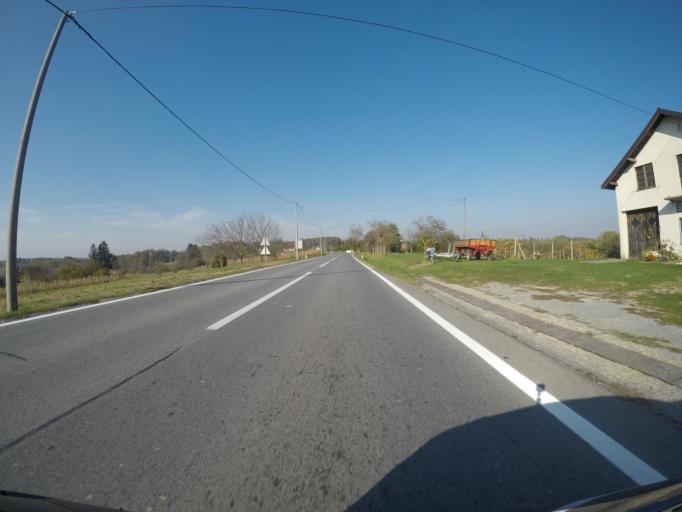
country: HR
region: Bjelovarsko-Bilogorska
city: Bjelovar
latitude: 45.9752
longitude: 16.8954
